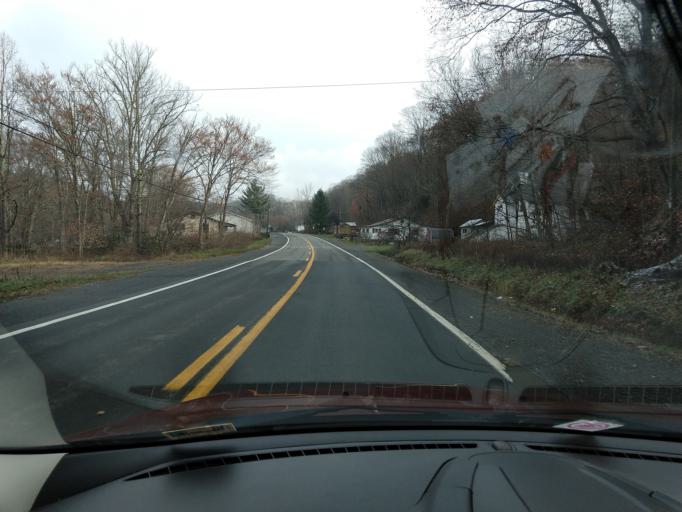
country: US
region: West Virginia
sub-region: Greenbrier County
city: Rainelle
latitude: 38.0415
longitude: -80.7265
